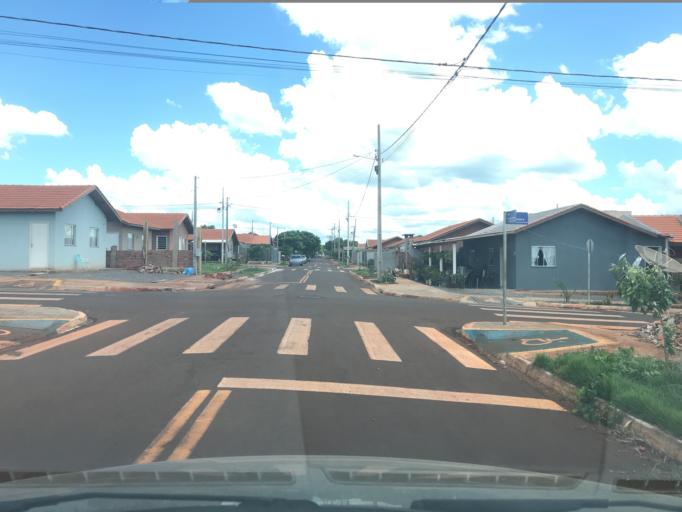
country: BR
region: Parana
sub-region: Palotina
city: Palotina
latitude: -24.2660
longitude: -53.8463
